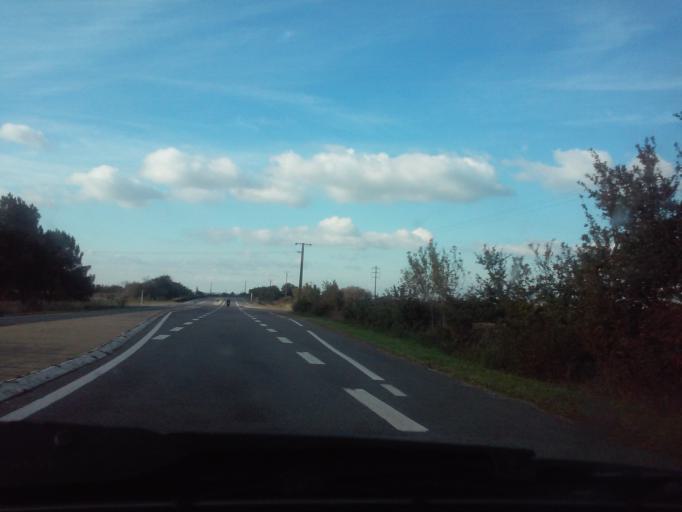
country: FR
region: Pays de la Loire
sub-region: Departement de la Loire-Atlantique
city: Saint-Viaud
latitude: 47.2665
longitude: -1.9848
